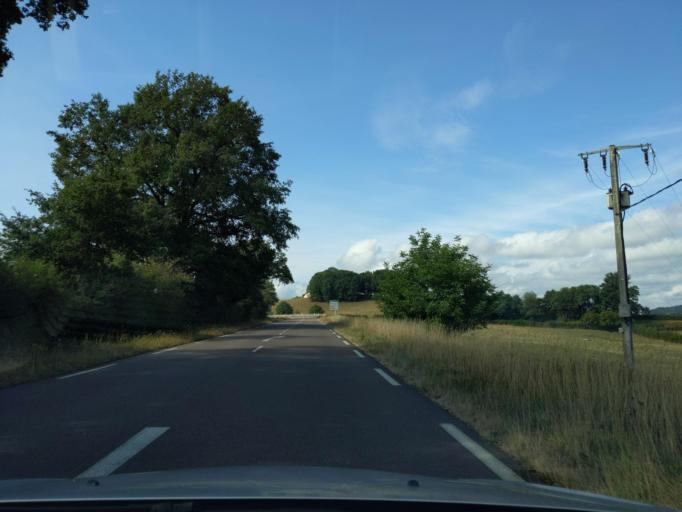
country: FR
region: Bourgogne
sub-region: Departement de Saone-et-Loire
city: Etang-sur-Arroux
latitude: 46.8930
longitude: 4.1522
